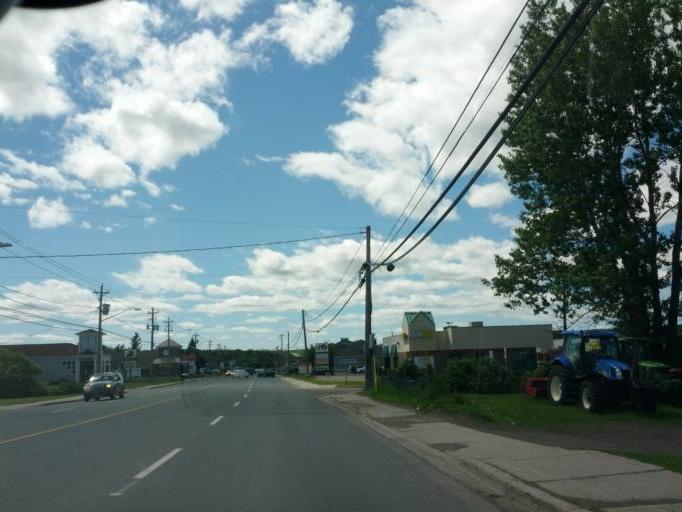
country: CA
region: New Brunswick
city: Moncton
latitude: 46.1217
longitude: -64.8478
